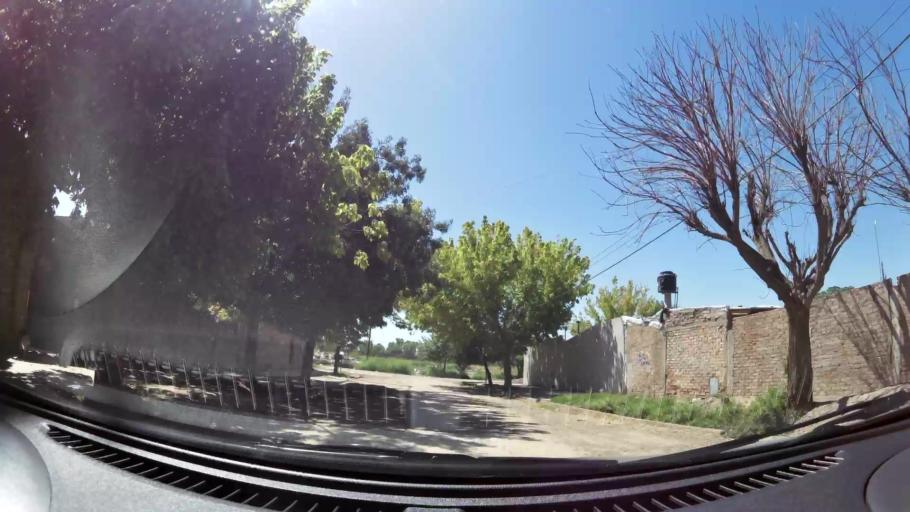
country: AR
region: Mendoza
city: Villa Nueva
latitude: -32.8735
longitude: -68.7983
